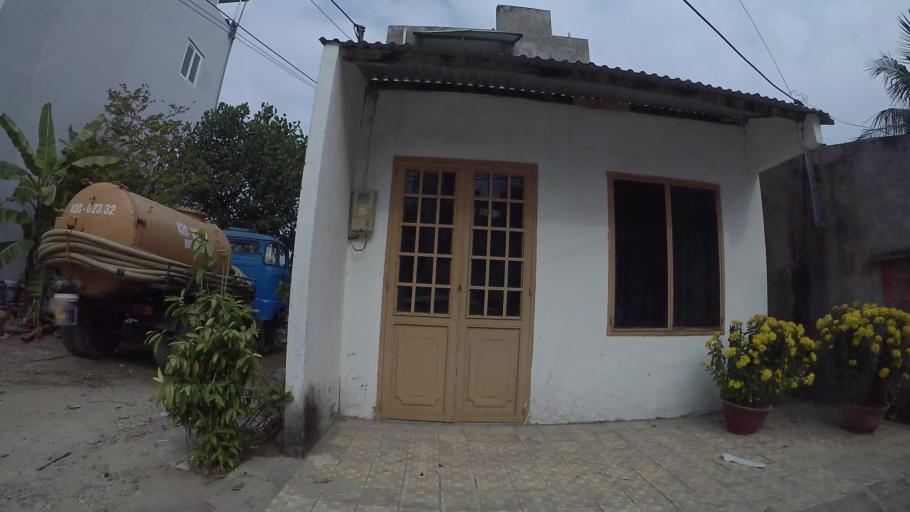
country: VN
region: Da Nang
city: Son Tra
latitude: 16.0683
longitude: 108.2392
